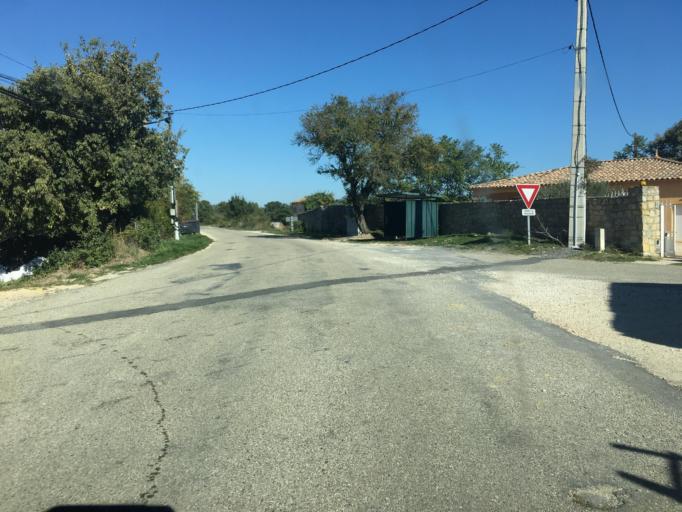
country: FR
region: Languedoc-Roussillon
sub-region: Departement du Gard
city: Barjac
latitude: 44.1648
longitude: 4.3157
